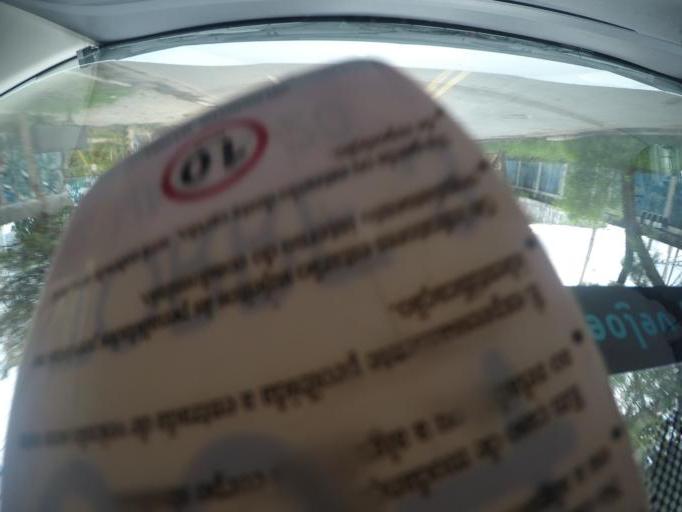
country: BR
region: Sao Paulo
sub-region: Sao Paulo
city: Sao Paulo
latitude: -23.5639
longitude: -46.6058
